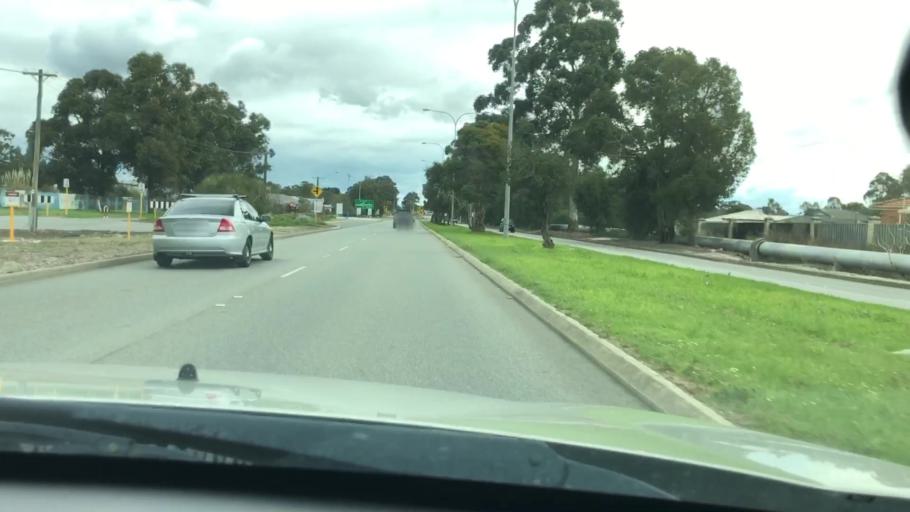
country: AU
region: Western Australia
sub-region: Armadale
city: Seville Grove
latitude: -32.1471
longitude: 115.9796
